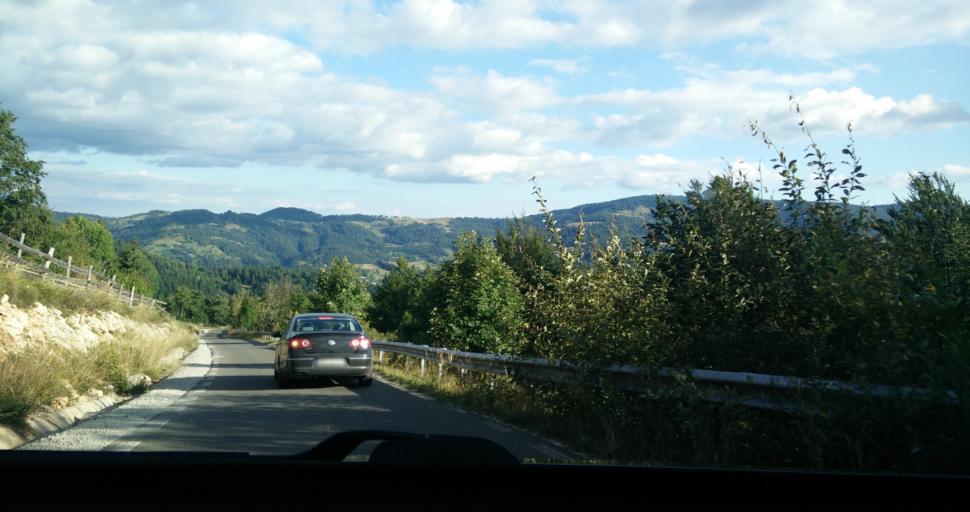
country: RO
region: Alba
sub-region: Comuna Scarisoara
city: Scarisoara
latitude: 46.4736
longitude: 22.8301
